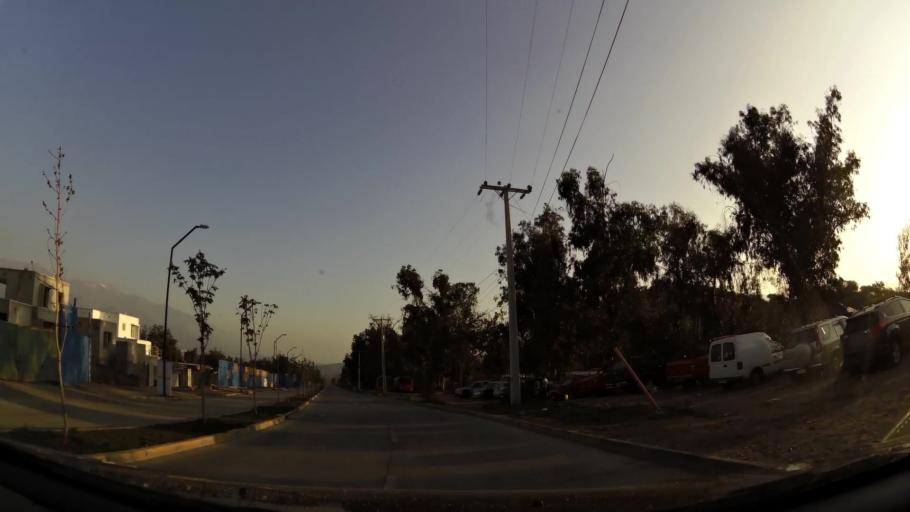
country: CL
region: Santiago Metropolitan
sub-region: Provincia de Chacabuco
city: Chicureo Abajo
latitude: -33.3233
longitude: -70.5191
